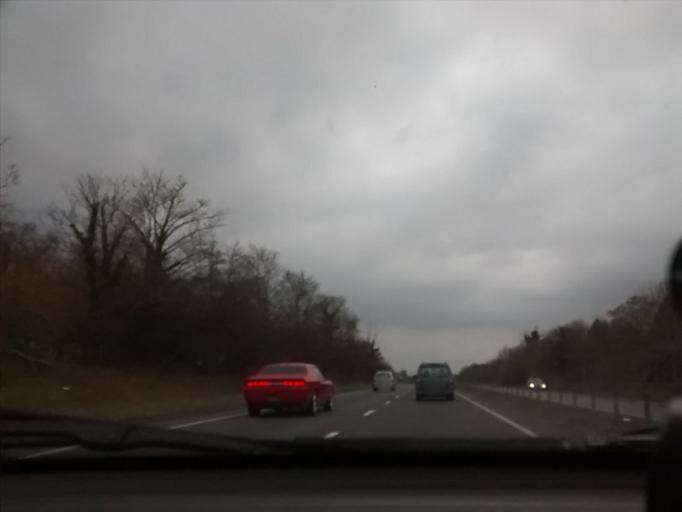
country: GB
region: England
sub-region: Cambridgeshire
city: Sawston
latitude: 52.1056
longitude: 0.2103
